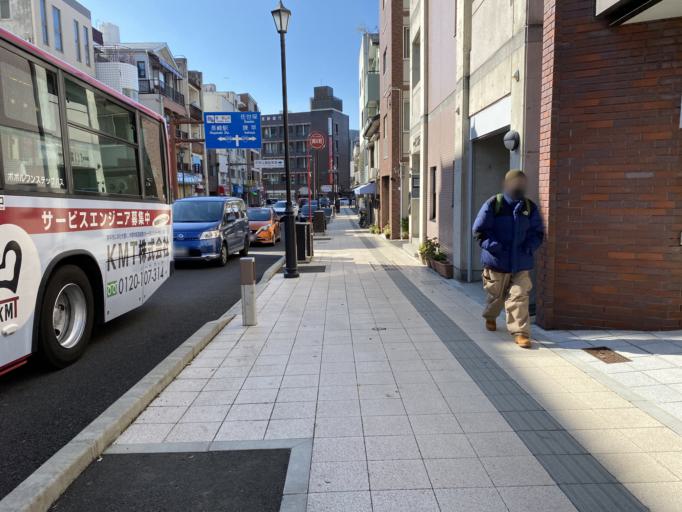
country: JP
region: Nagasaki
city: Nagasaki-shi
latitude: 32.7745
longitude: 129.8635
